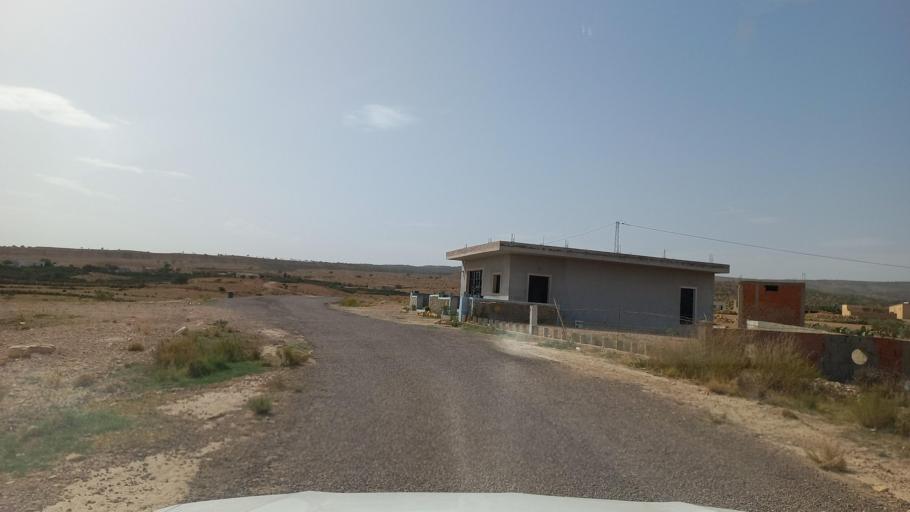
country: TN
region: Al Qasrayn
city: Kasserine
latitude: 35.3033
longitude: 8.9438
